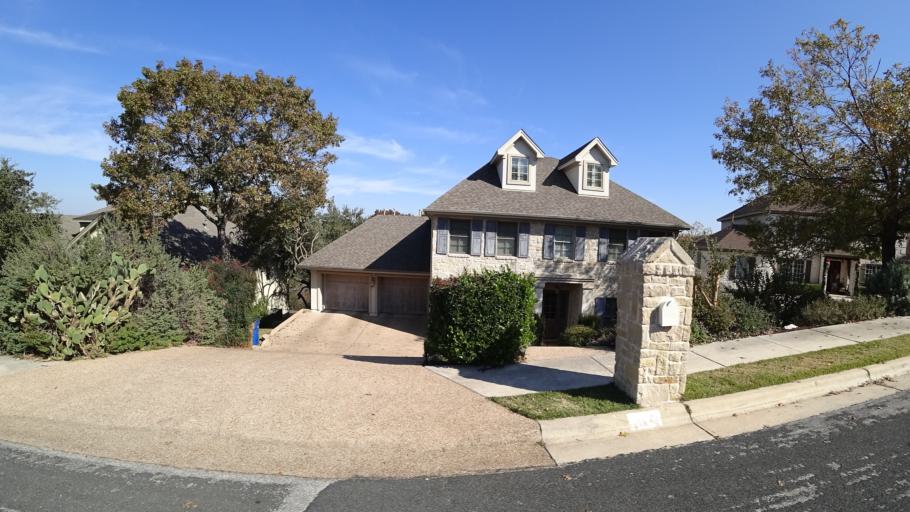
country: US
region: Texas
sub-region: Williamson County
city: Jollyville
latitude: 30.3716
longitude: -97.7654
